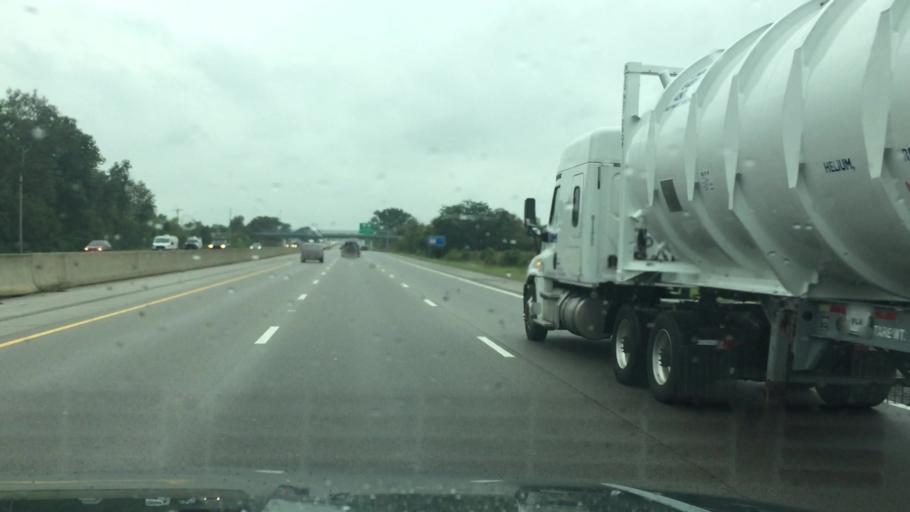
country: US
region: Ohio
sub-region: Clark County
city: Crystal Lakes
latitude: 39.8648
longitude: -84.0275
